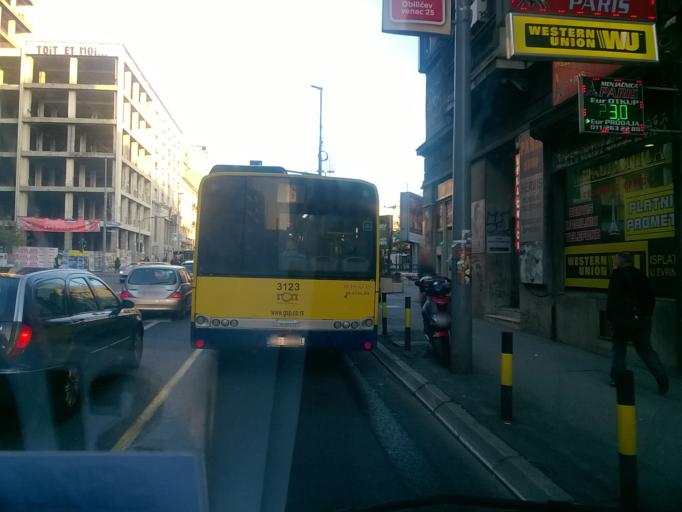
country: RS
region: Central Serbia
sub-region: Belgrade
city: Stari Grad
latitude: 44.8146
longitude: 20.4560
